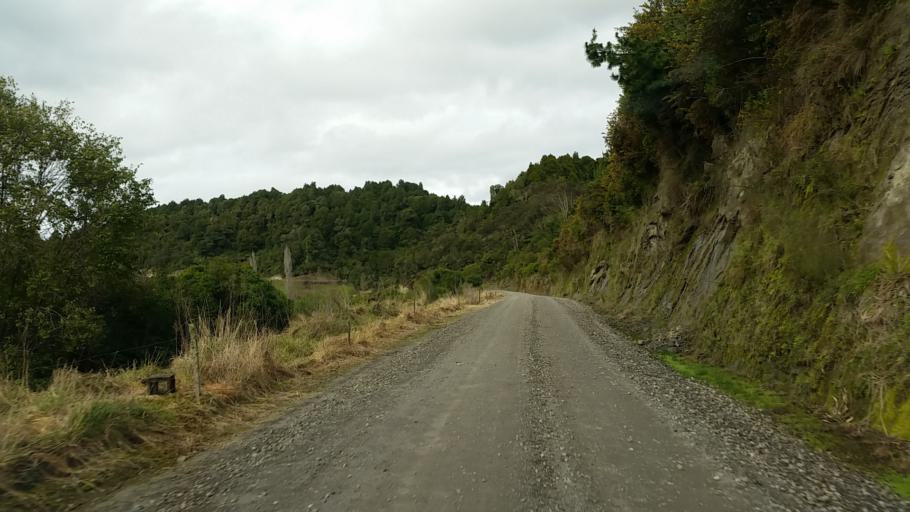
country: NZ
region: Taranaki
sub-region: New Plymouth District
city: Waitara
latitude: -39.1574
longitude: 174.5264
